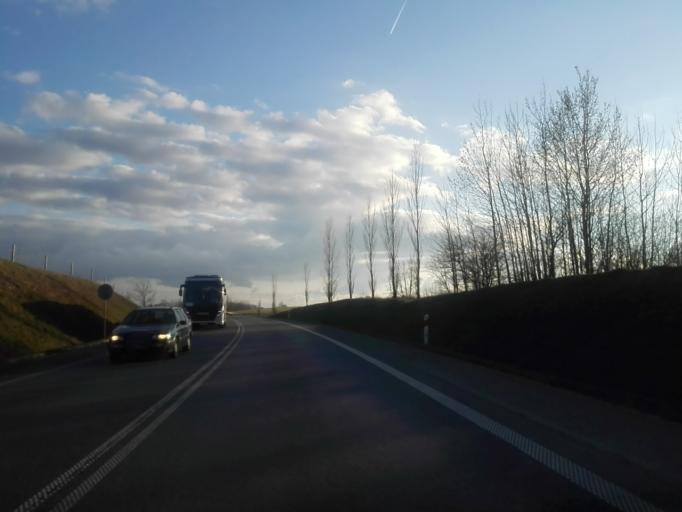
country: PL
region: Podlasie
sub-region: Suwalki
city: Suwalki
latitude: 54.1943
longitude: 23.0124
